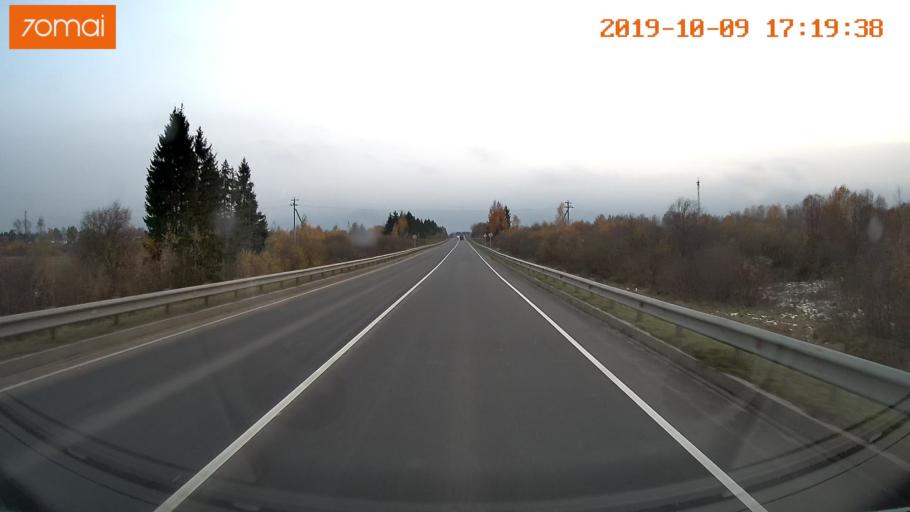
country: RU
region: Ivanovo
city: Furmanov
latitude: 57.2438
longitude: 41.1506
